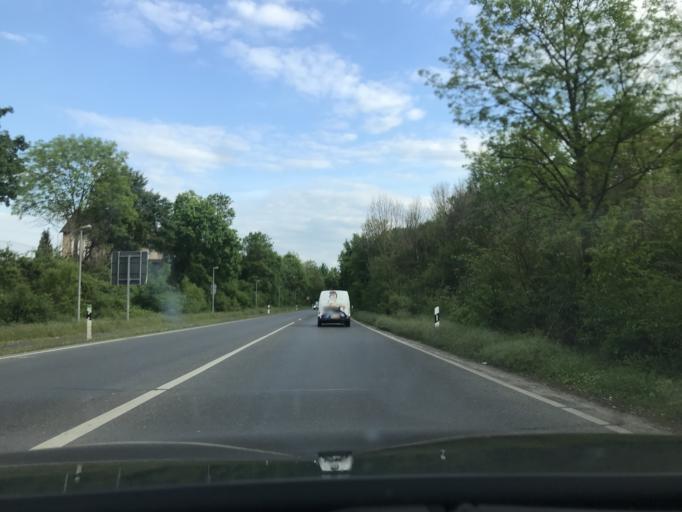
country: DE
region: North Rhine-Westphalia
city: Wesseling
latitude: 50.8269
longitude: 6.9605
